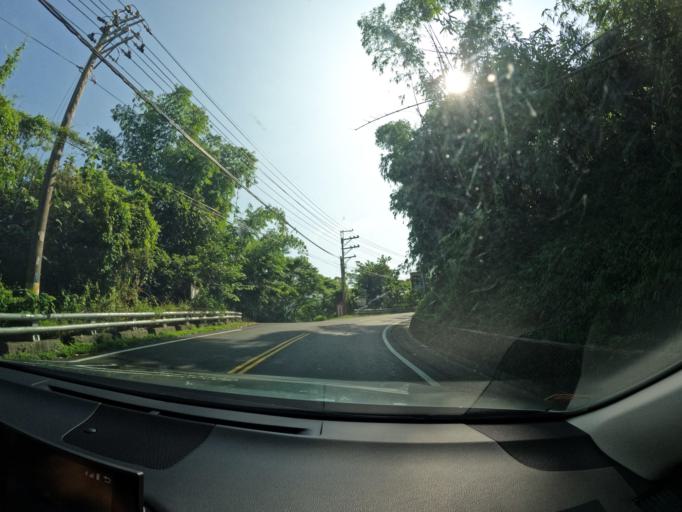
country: TW
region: Taiwan
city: Yujing
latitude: 23.0779
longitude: 120.6210
